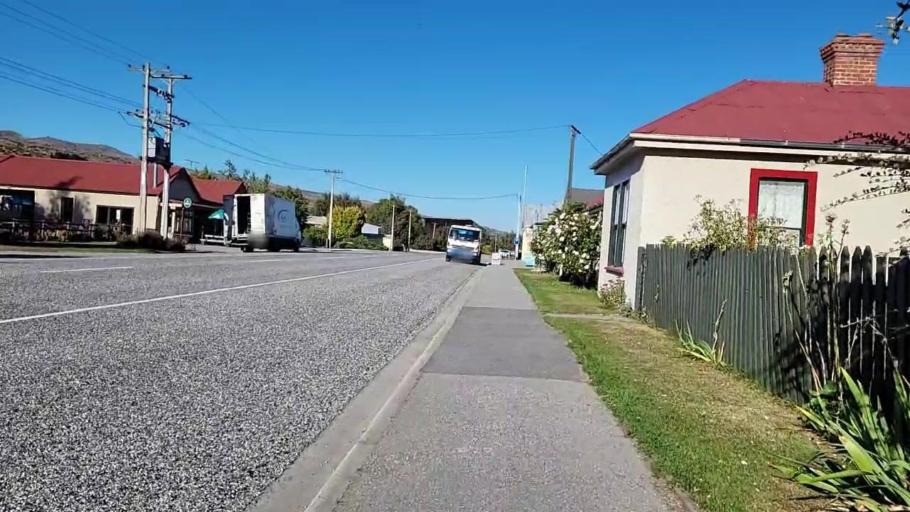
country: NZ
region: Otago
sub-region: Queenstown-Lakes District
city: Wanaka
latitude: -45.0065
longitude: 169.9133
